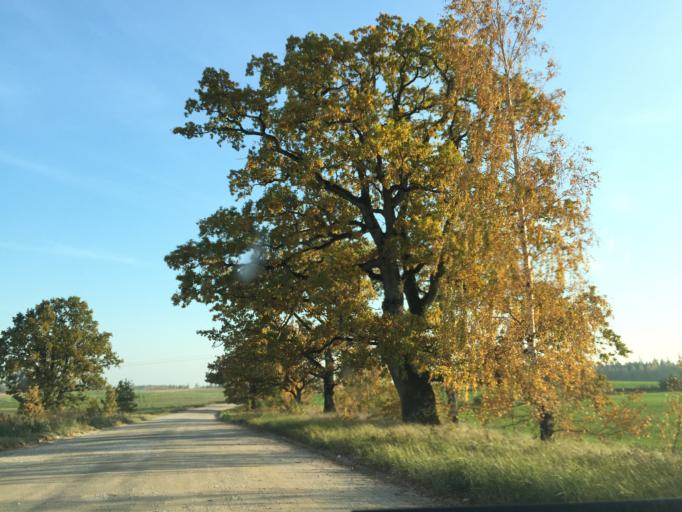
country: LV
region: Vainode
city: Vainode
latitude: 56.6164
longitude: 21.8148
